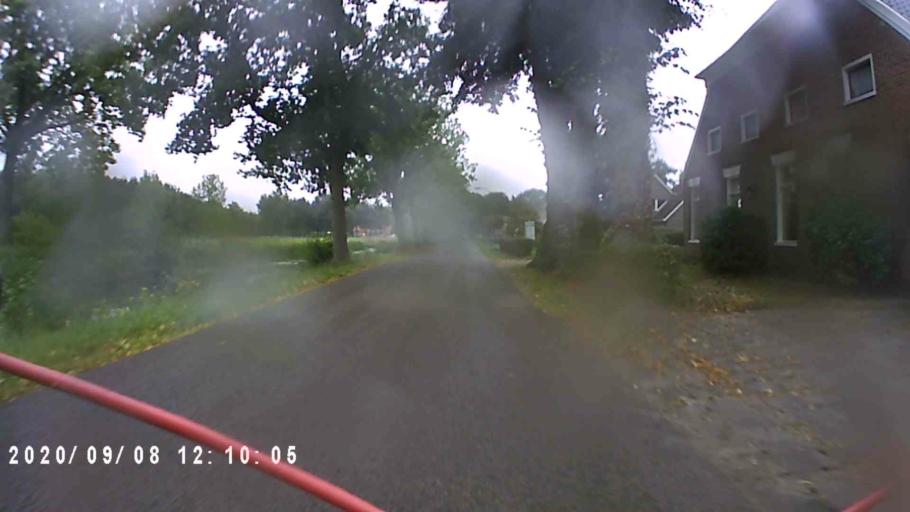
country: NL
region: Groningen
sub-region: Gemeente Veendam
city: Veendam
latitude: 53.0978
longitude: 6.8331
